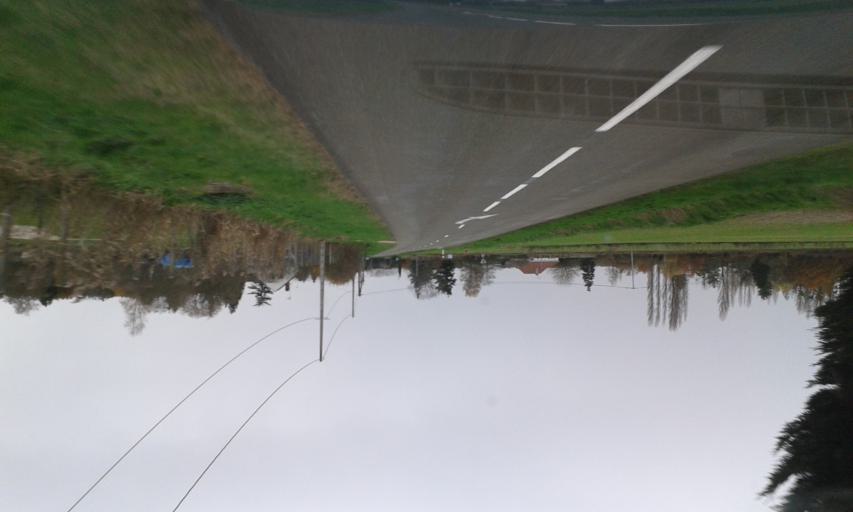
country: FR
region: Centre
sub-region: Departement du Loiret
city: Vitry-aux-Loges
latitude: 47.9297
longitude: 2.2182
